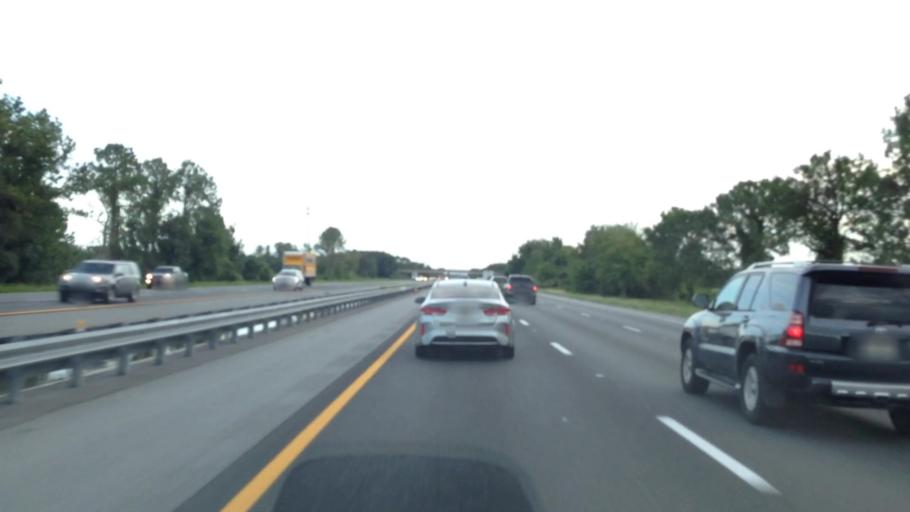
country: US
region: Florida
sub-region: Sumter County
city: Lake Panasoffkee
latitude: 28.8054
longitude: -82.0885
